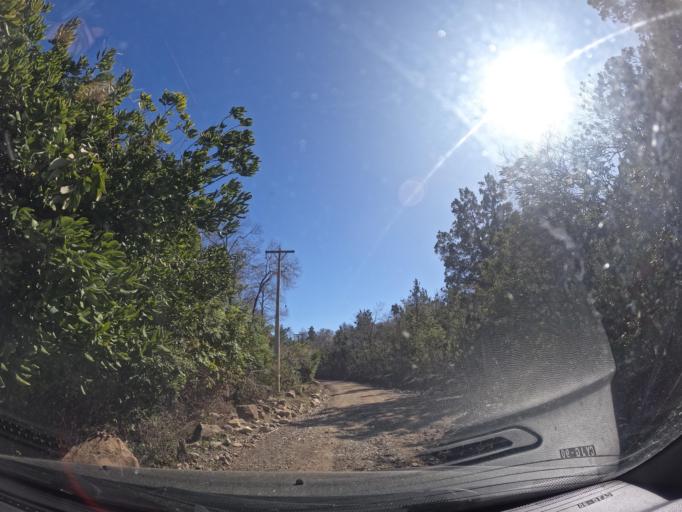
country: CL
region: Maule
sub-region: Provincia de Linares
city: Longavi
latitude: -36.2457
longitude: -71.3417
